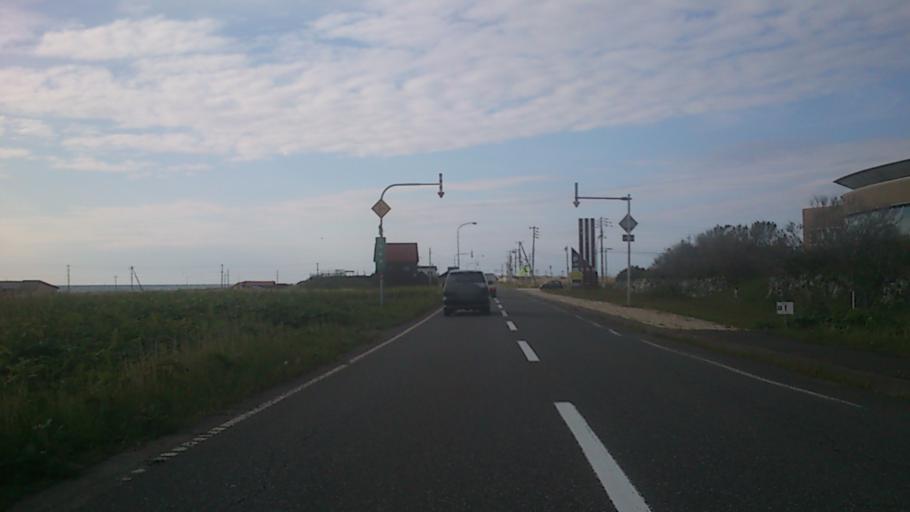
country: JP
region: Hokkaido
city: Wakkanai
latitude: 45.4203
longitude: 141.6370
